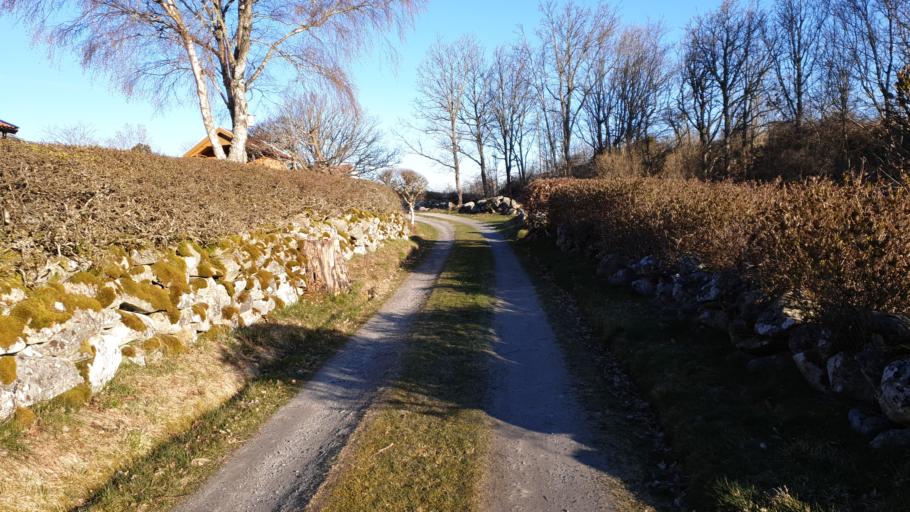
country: SE
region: Vaestra Goetaland
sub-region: Lysekils Kommun
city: Lysekil
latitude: 58.1643
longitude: 11.4377
